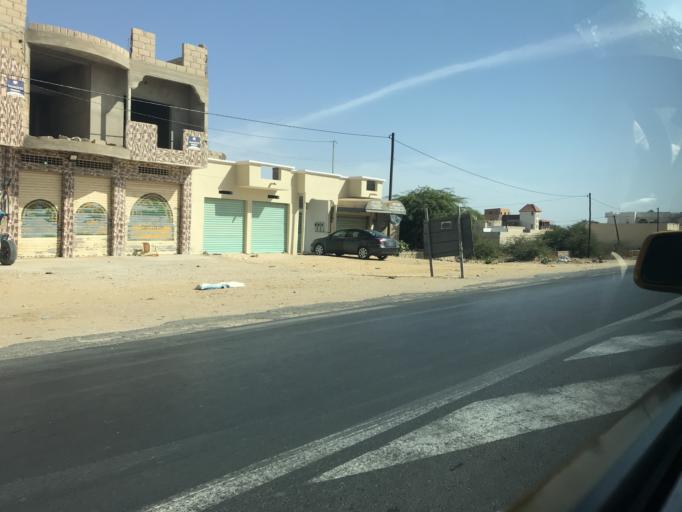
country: SN
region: Saint-Louis
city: Saint-Louis
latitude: 16.0551
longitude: -16.4270
